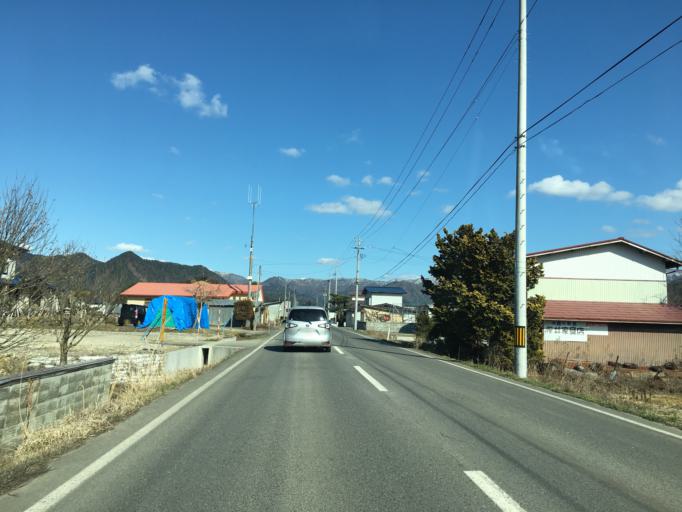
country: JP
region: Yamagata
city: Takahata
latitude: 37.9538
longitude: 140.1741
